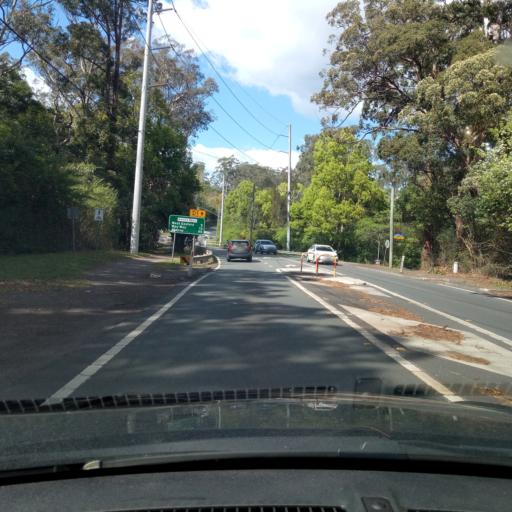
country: AU
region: New South Wales
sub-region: Gosford Shire
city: Narara
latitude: -33.4007
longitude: 151.3426
